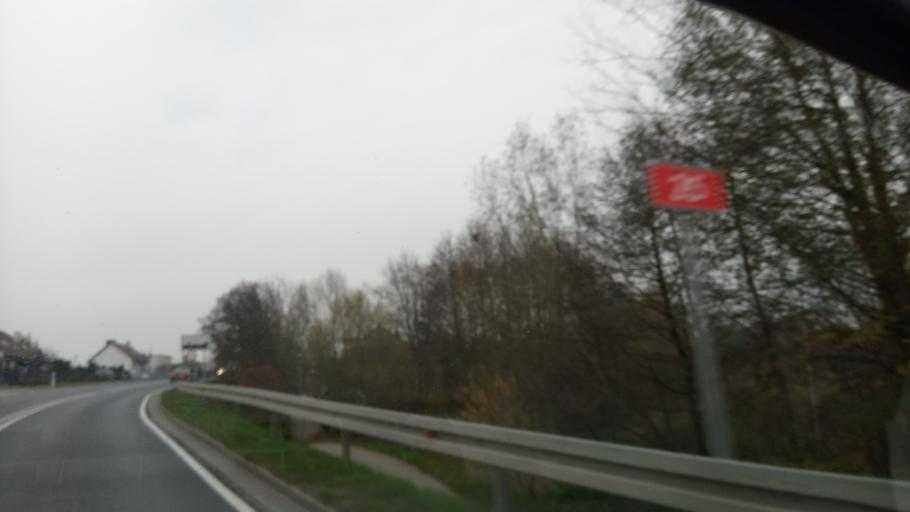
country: PL
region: Kujawsko-Pomorskie
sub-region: Powiat sepolenski
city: Sepolno Krajenskie
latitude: 53.4669
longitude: 17.5283
